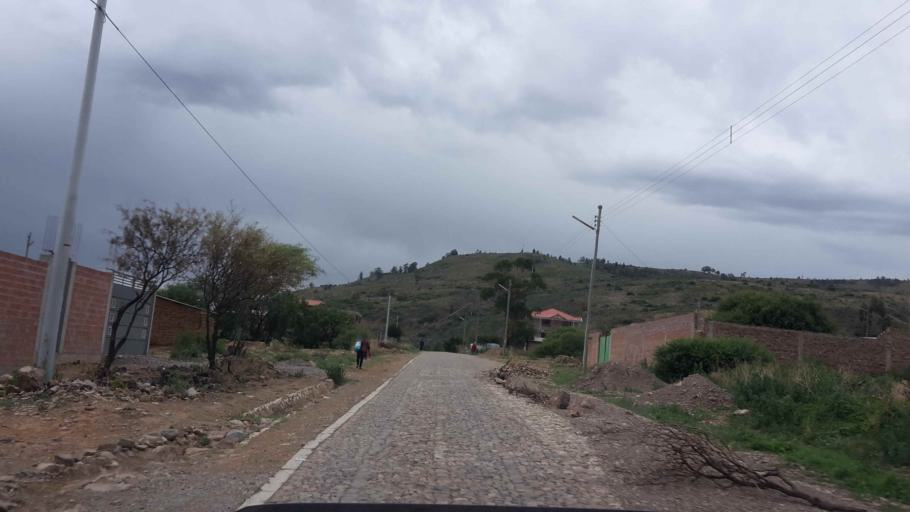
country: BO
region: Cochabamba
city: Cochabamba
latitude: -17.5364
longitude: -66.2030
